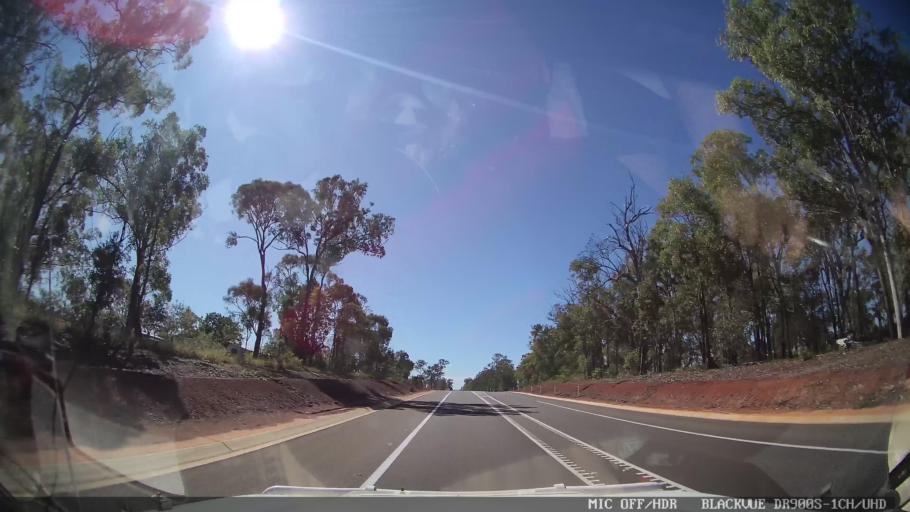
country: AU
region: Queensland
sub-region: Fraser Coast
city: Maryborough
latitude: -25.6525
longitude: 152.6313
